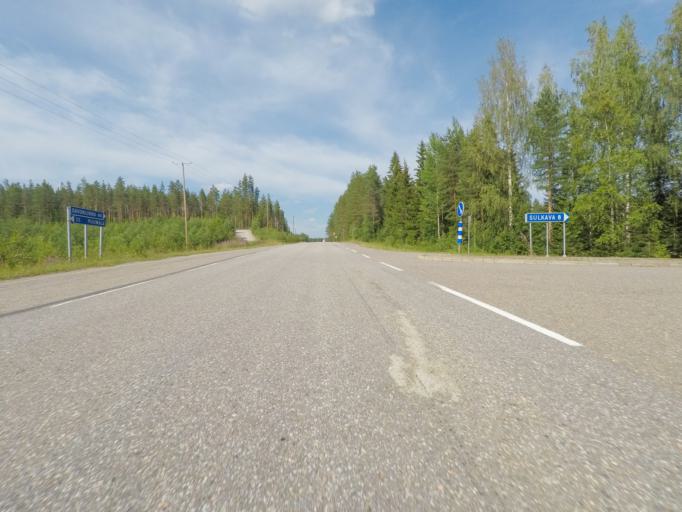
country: FI
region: Southern Savonia
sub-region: Savonlinna
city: Sulkava
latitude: 61.7831
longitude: 28.2402
